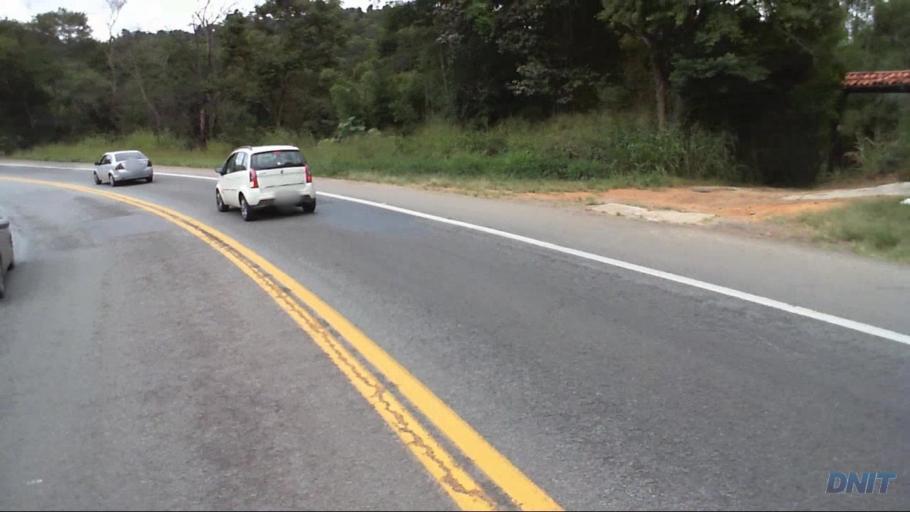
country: BR
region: Minas Gerais
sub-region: Caete
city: Caete
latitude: -19.7505
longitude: -43.6264
